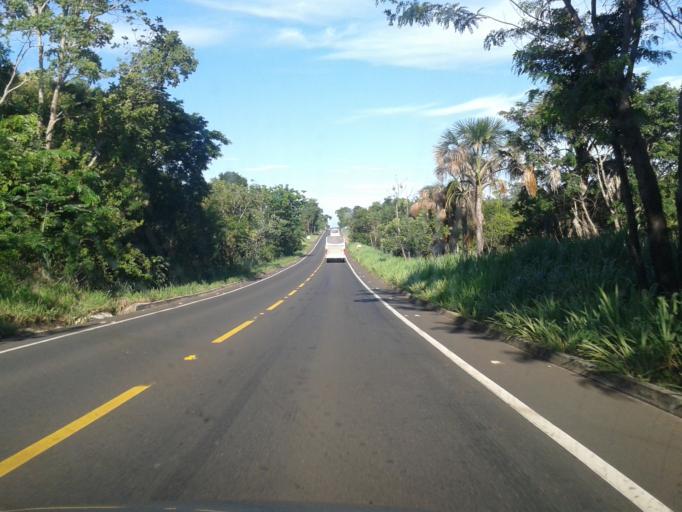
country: BR
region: Goias
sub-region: Caldas Novas
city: Caldas Novas
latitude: -18.1151
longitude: -48.6071
